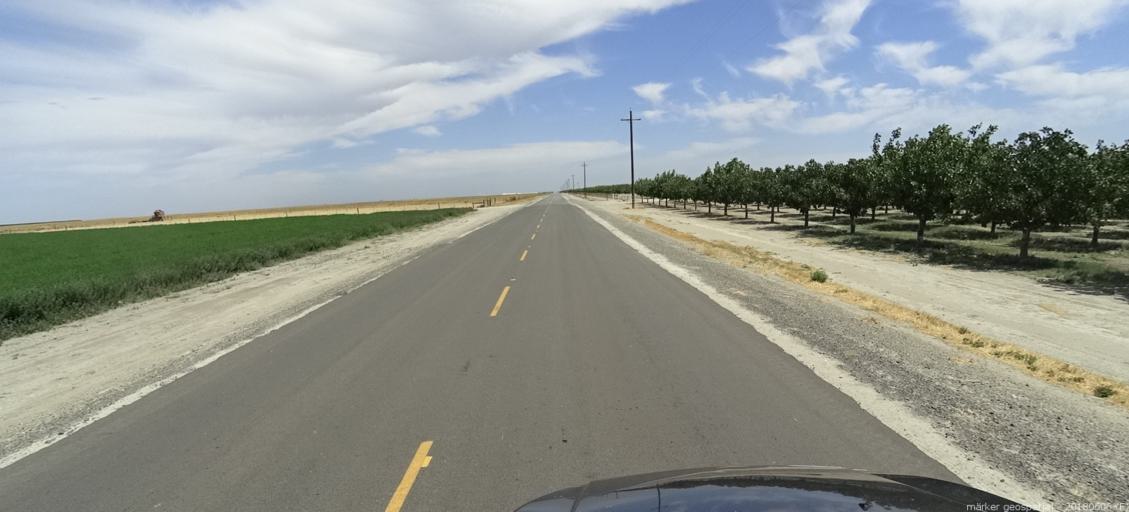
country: US
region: California
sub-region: Fresno County
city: Firebaugh
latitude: 36.8792
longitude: -120.3819
